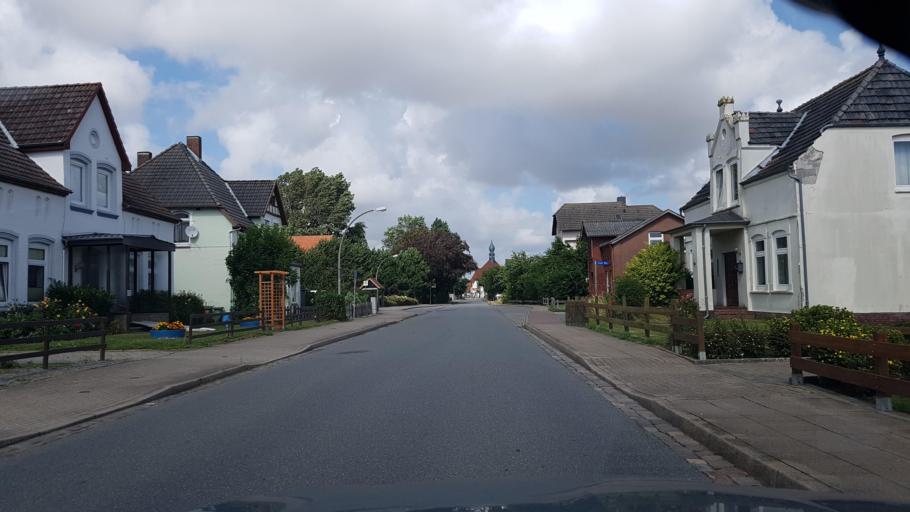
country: DE
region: Schleswig-Holstein
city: Suderdeich
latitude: 54.2078
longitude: 8.9168
